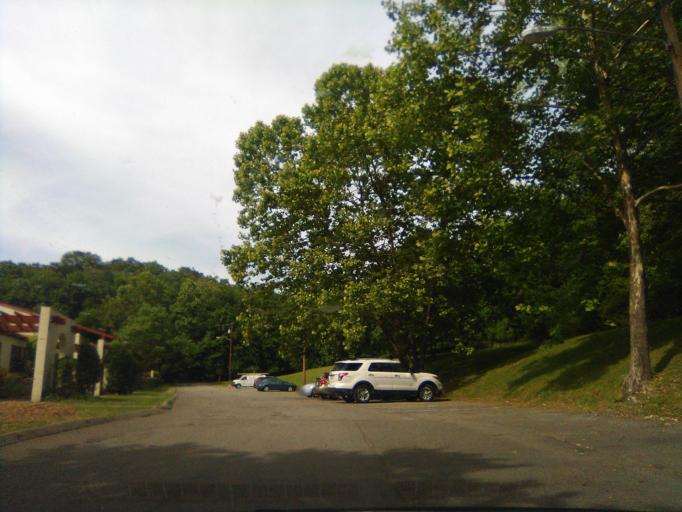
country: US
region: Tennessee
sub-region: Davidson County
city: Belle Meade
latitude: 36.0830
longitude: -86.9144
